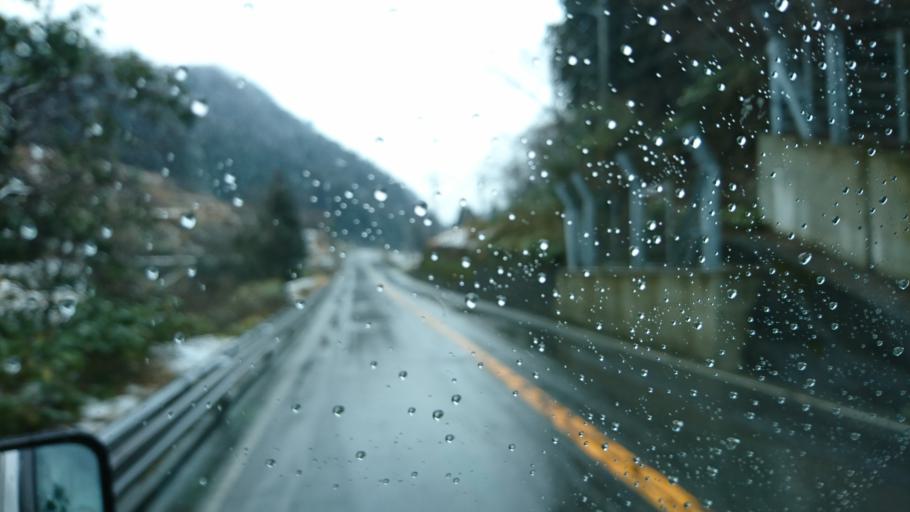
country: JP
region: Tottori
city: Tottori
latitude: 35.5394
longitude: 134.5094
